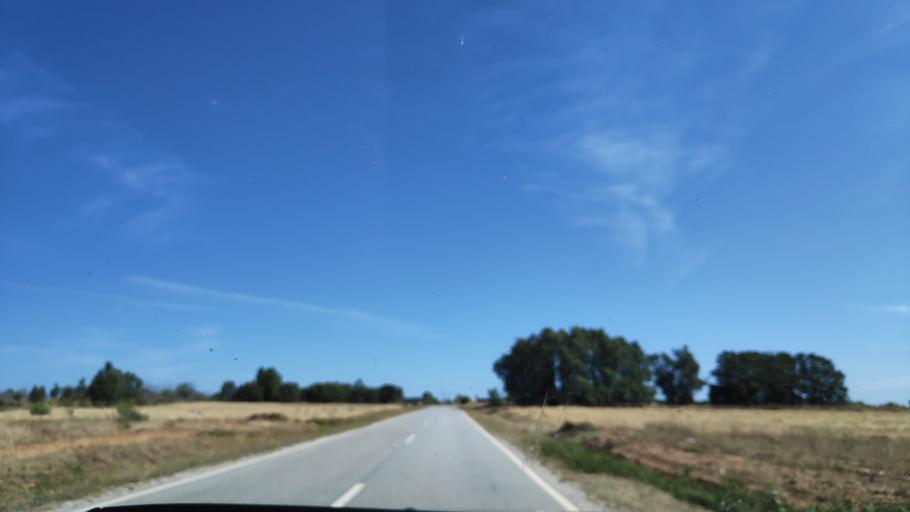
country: ES
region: Castille and Leon
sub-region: Provincia de Zamora
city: Alcanices
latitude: 41.5834
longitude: -6.3553
